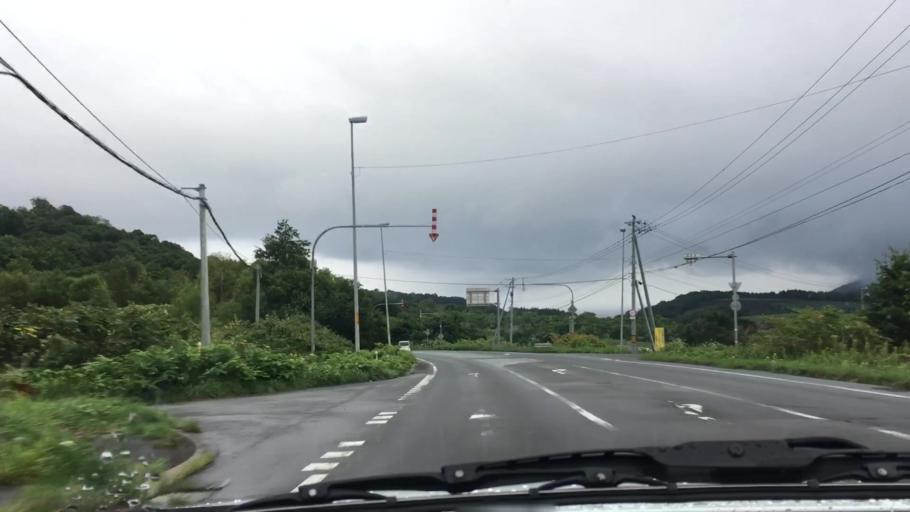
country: JP
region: Hokkaido
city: Niseko Town
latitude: 42.6056
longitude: 140.7274
